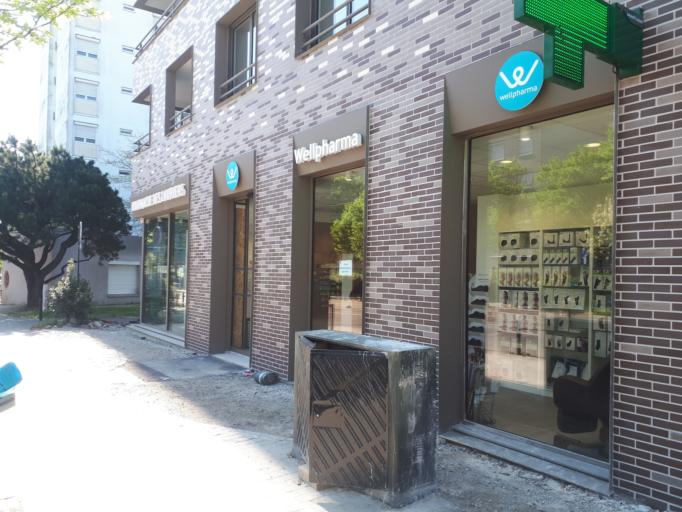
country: FR
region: Pays de la Loire
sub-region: Departement de la Loire-Atlantique
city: Bouguenais
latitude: 47.2051
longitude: -1.6060
